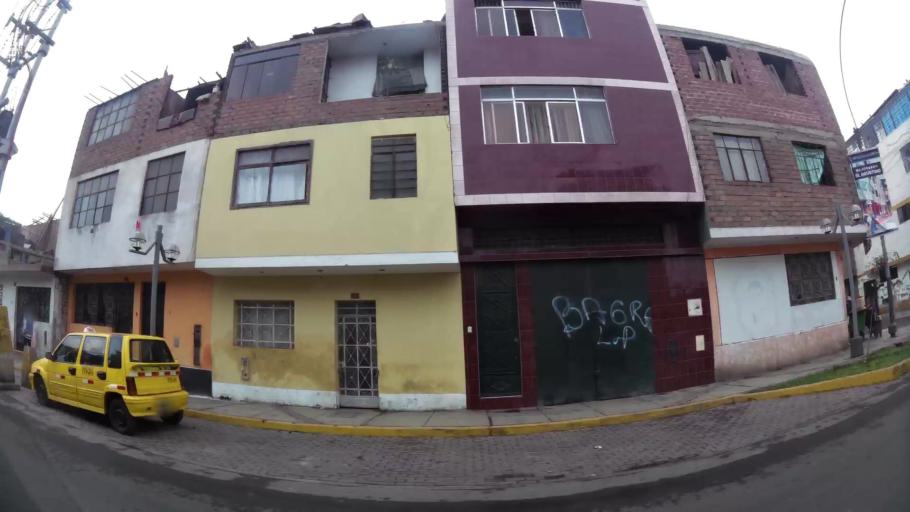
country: PE
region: Lima
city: Lima
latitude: -12.0510
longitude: -77.0052
